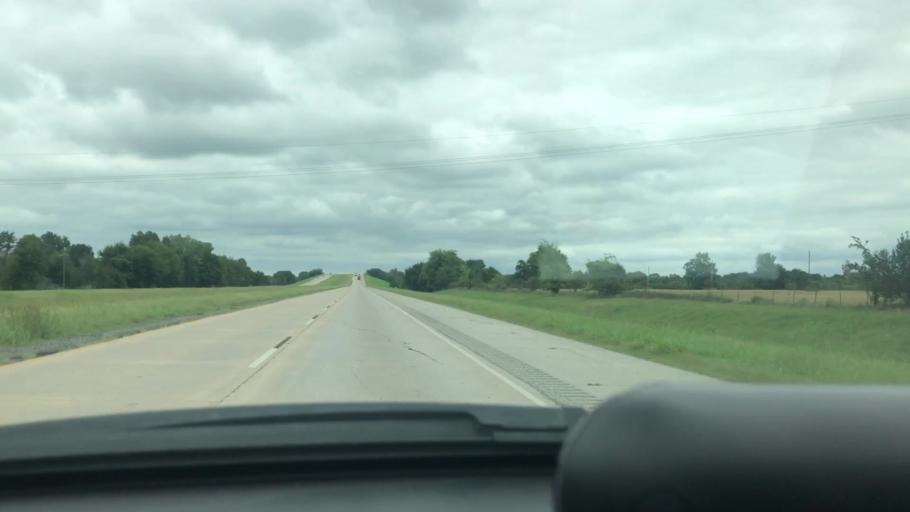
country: US
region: Oklahoma
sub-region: Wagoner County
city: Wagoner
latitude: 35.8748
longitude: -95.4019
